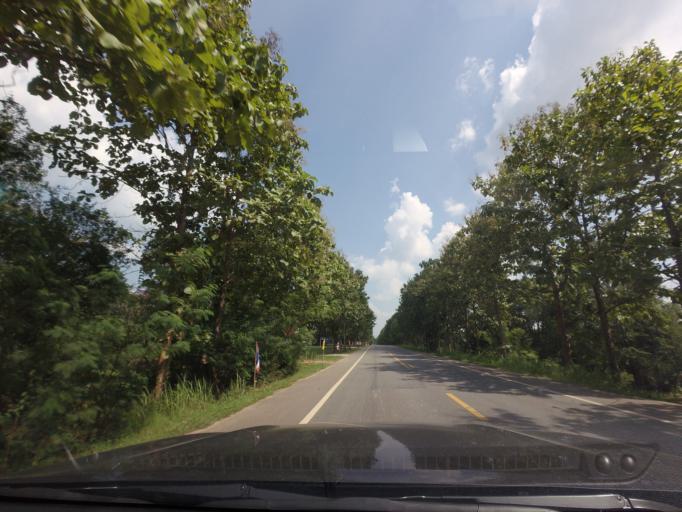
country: TH
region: Phitsanulok
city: Chat Trakan
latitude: 17.2840
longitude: 100.5259
